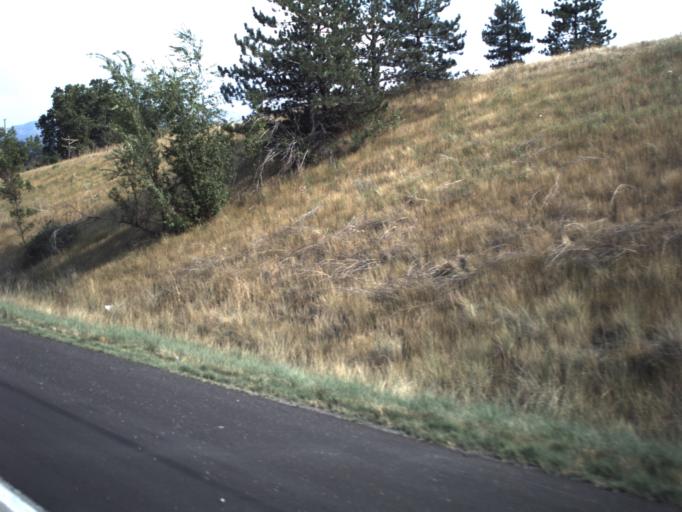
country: US
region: Utah
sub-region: Salt Lake County
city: Willard
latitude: 40.7193
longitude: -111.8457
